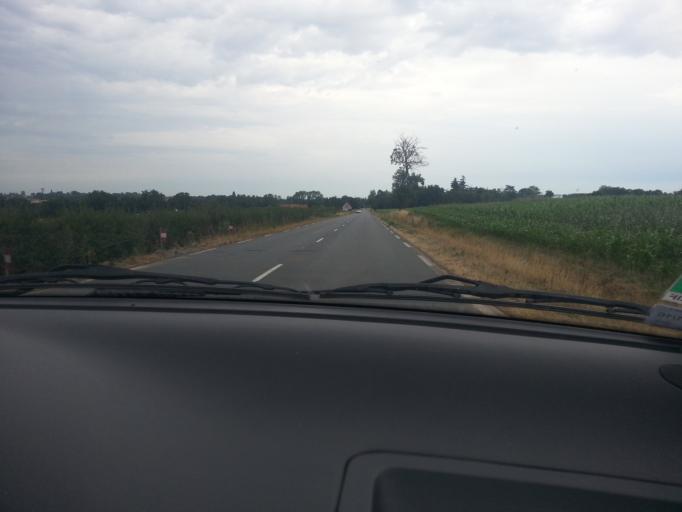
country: FR
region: Auvergne
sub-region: Departement de l'Allier
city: Saint-Gerand-le-Puy
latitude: 46.2002
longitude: 3.4972
